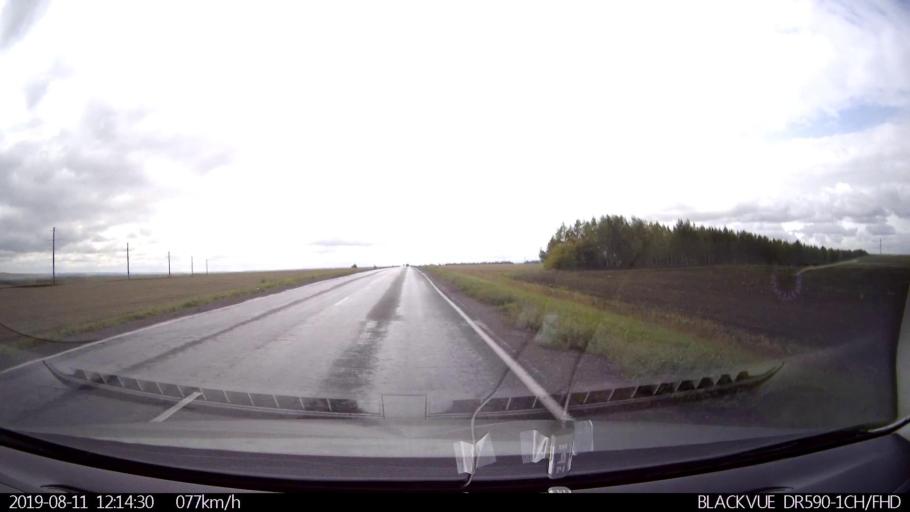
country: RU
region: Ulyanovsk
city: Ignatovka
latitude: 53.9517
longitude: 47.9793
